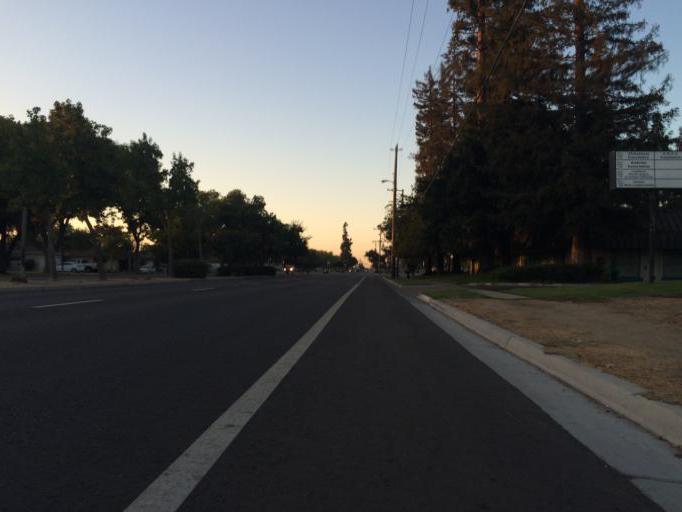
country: US
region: California
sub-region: Fresno County
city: Tarpey Village
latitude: 36.7985
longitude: -119.7544
